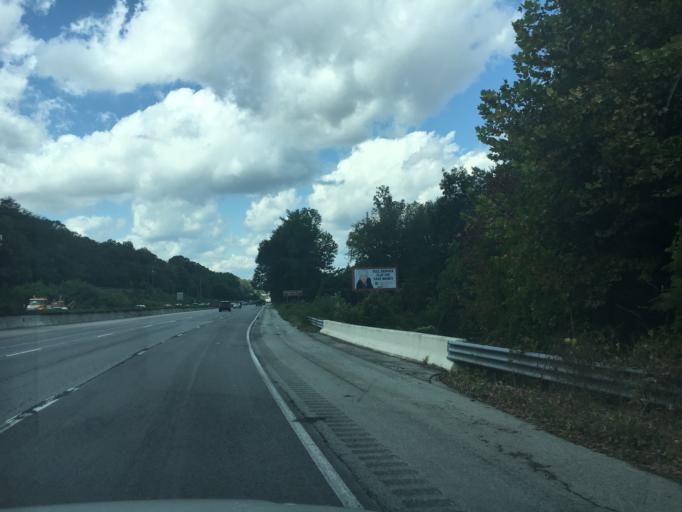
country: US
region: South Carolina
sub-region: Greenville County
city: Greenville
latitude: 34.8517
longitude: -82.3696
